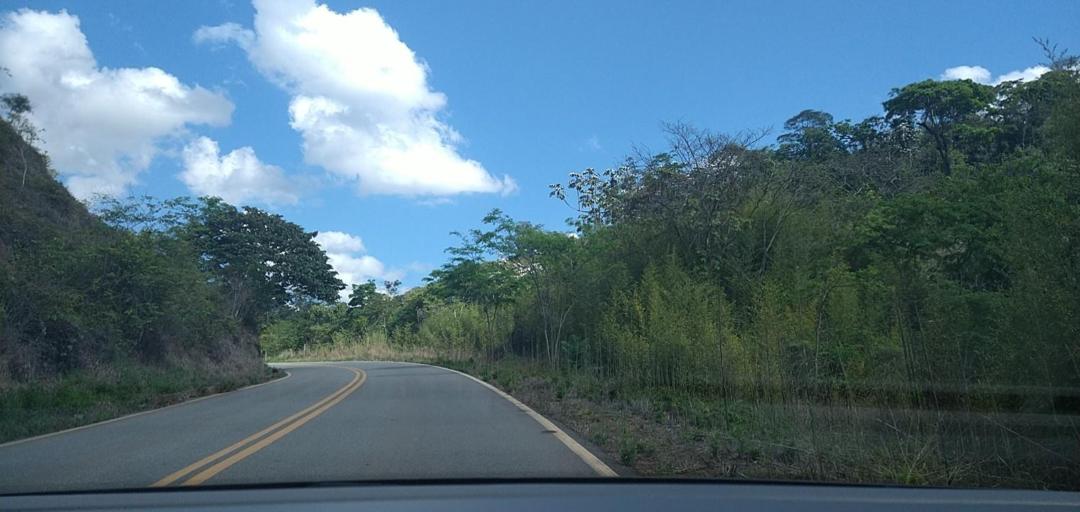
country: BR
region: Minas Gerais
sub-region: Rio Piracicaba
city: Rio Piracicaba
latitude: -19.9962
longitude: -43.1115
